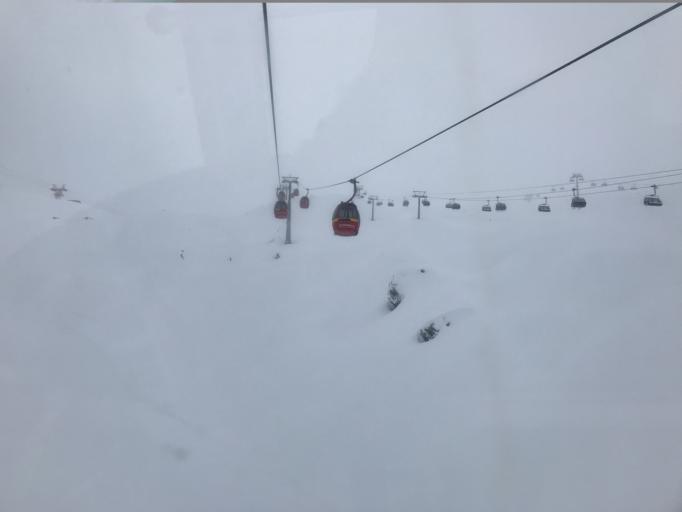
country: AT
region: Salzburg
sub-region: Politischer Bezirk Zell am See
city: Piesendorf
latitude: 47.2156
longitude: 12.6955
